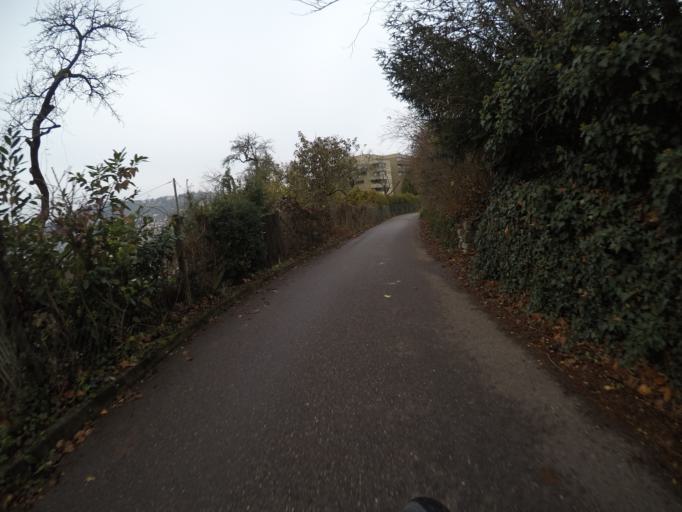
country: DE
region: Baden-Wuerttemberg
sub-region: Regierungsbezirk Stuttgart
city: Stuttgart
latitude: 48.7583
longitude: 9.1642
